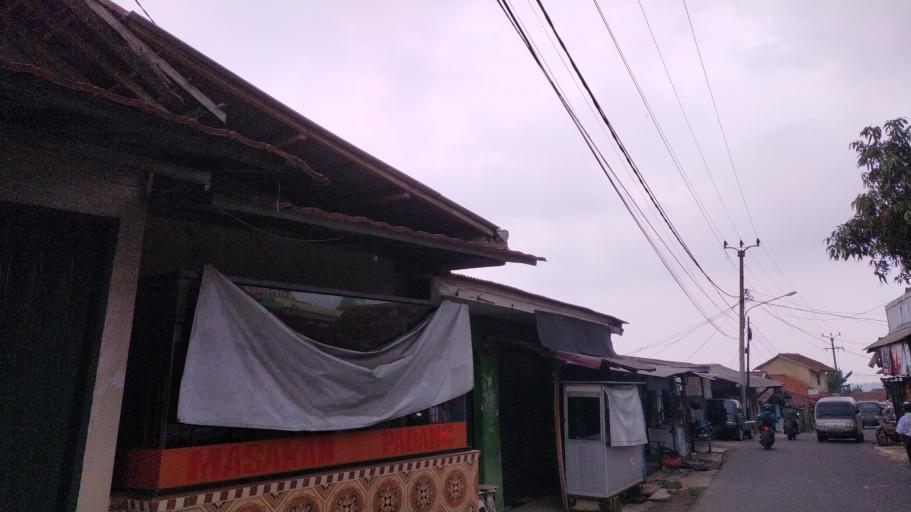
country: ID
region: West Java
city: Ciampea
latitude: -6.6131
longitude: 106.6962
